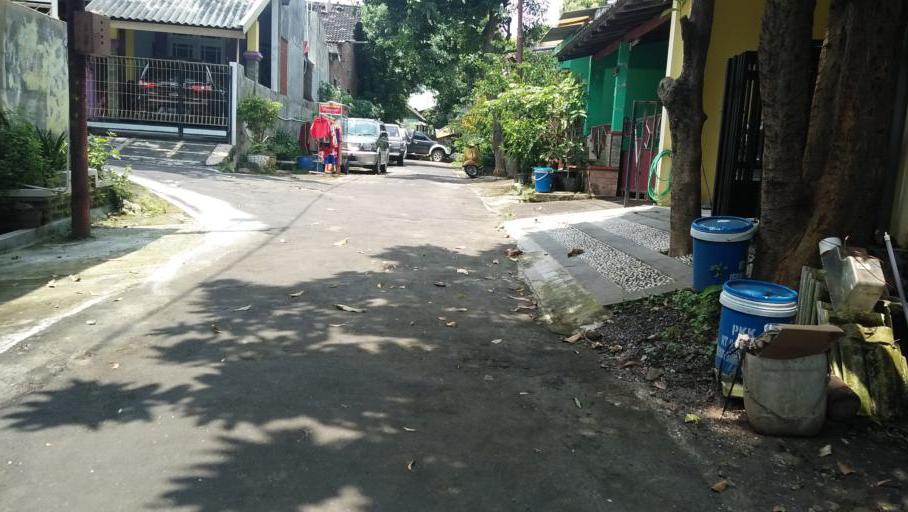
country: ID
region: Central Java
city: Semarang
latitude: -7.0347
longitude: 110.4542
